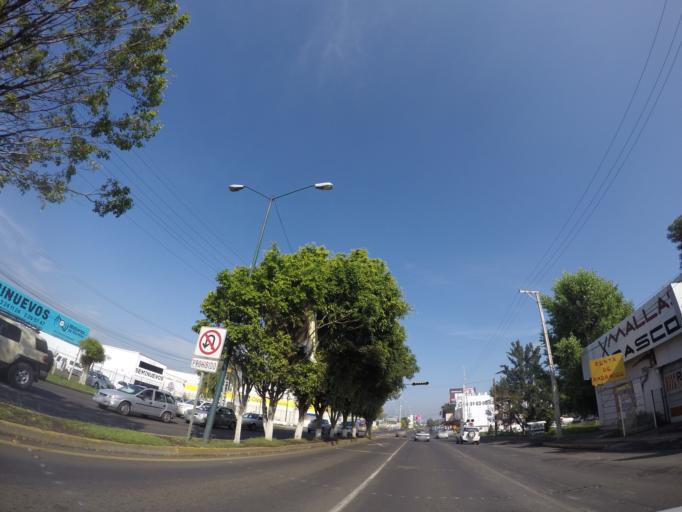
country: MX
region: Michoacan
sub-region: Morelia
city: Morelos
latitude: 19.6775
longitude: -101.2312
